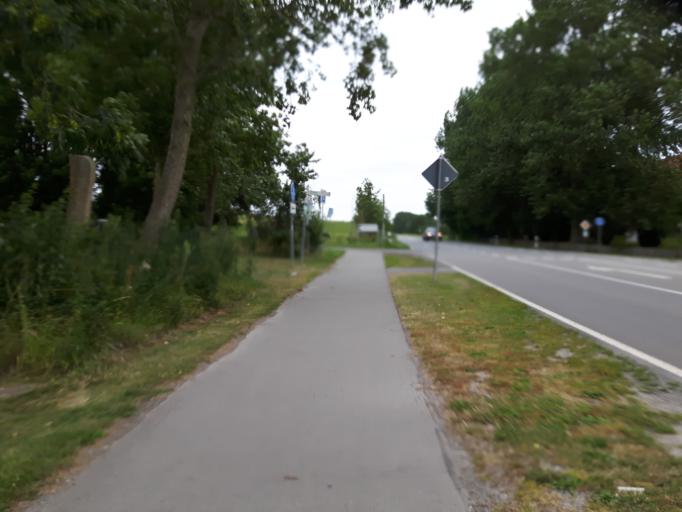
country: DE
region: Lower Saxony
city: Varel
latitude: 53.3947
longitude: 8.2607
